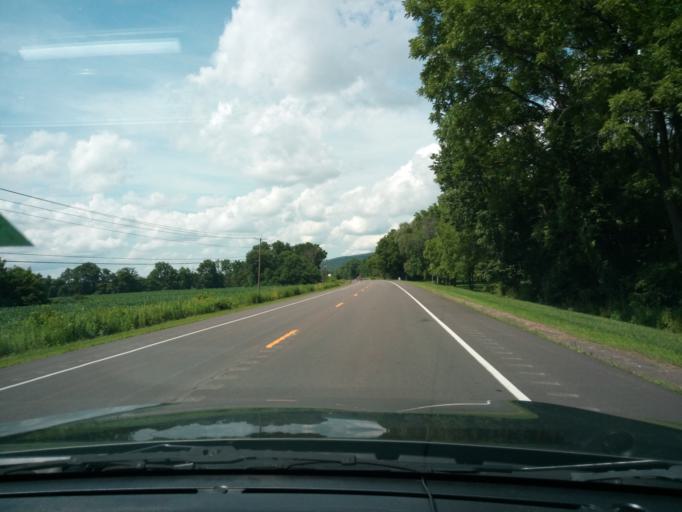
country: US
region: New York
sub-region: Chemung County
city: Southport
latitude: 42.0281
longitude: -76.7419
